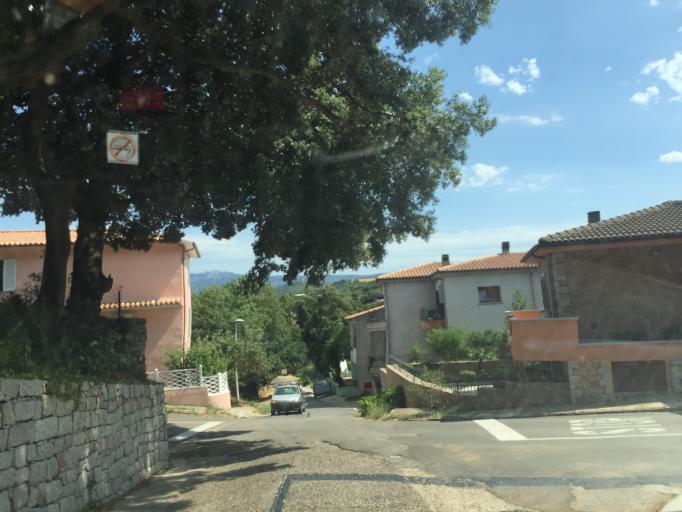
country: IT
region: Sardinia
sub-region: Provincia di Olbia-Tempio
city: Aggius
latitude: 40.9280
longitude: 9.0662
